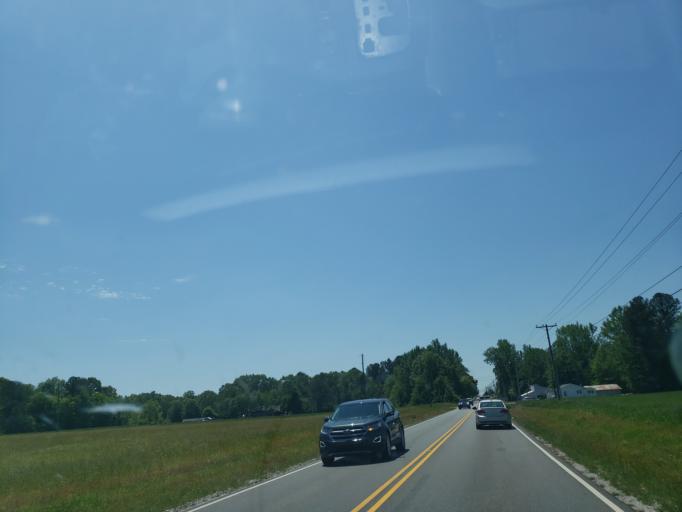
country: US
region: Alabama
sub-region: Madison County
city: Harvest
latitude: 34.8831
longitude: -86.7396
